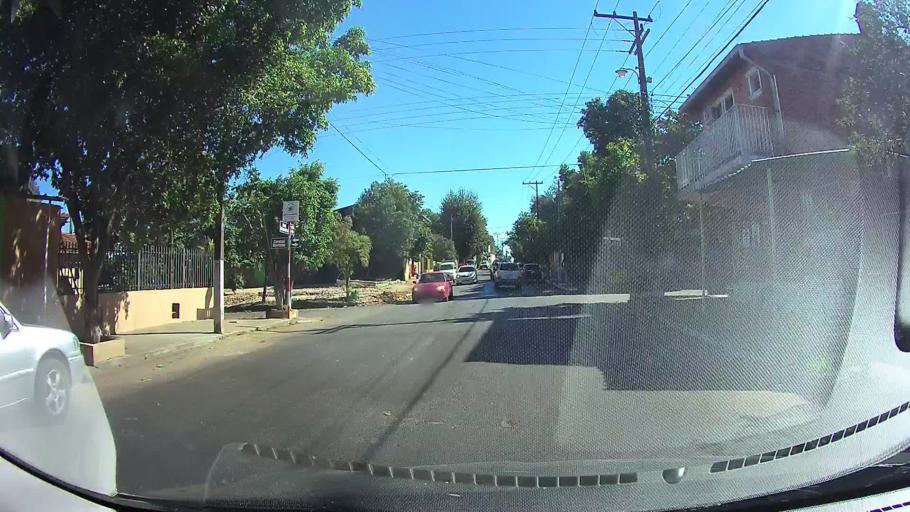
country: PY
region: Central
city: Villa Elisa
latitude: -25.3490
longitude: -57.5795
